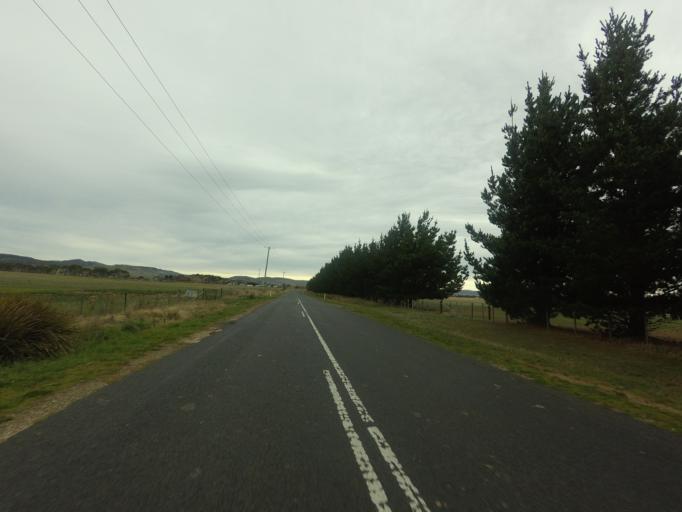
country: AU
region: Tasmania
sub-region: Derwent Valley
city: New Norfolk
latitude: -42.3967
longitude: 147.0053
